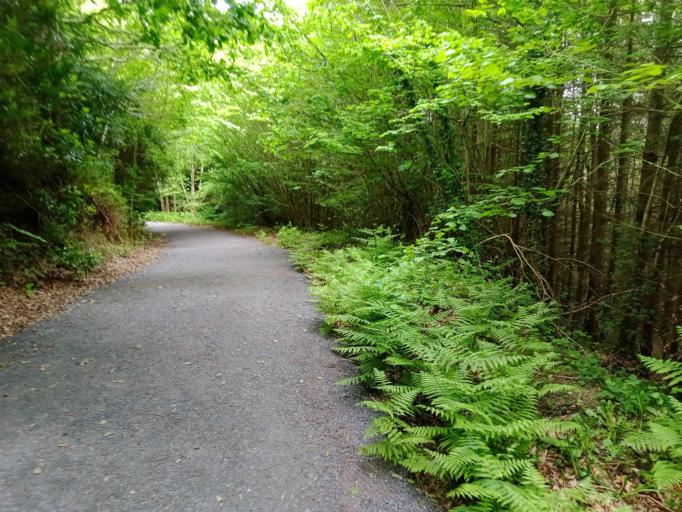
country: IE
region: Leinster
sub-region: Kilkenny
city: Thomastown
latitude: 52.4728
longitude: -7.0467
